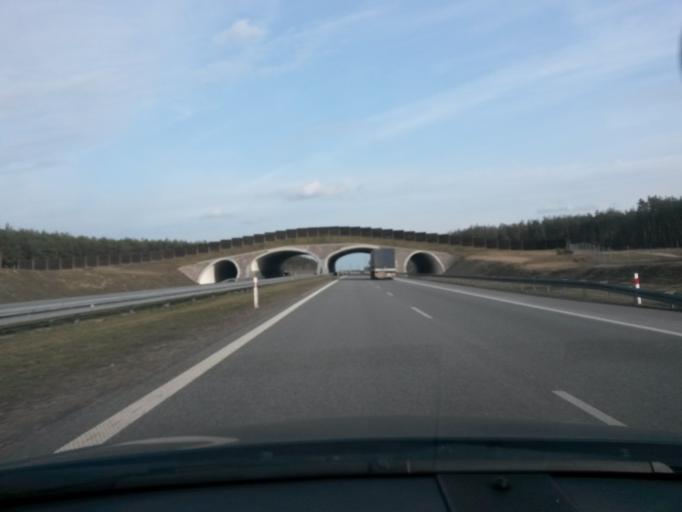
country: PL
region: Greater Poland Voivodeship
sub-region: Powiat turecki
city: Tuliszkow
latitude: 52.1454
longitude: 18.3184
